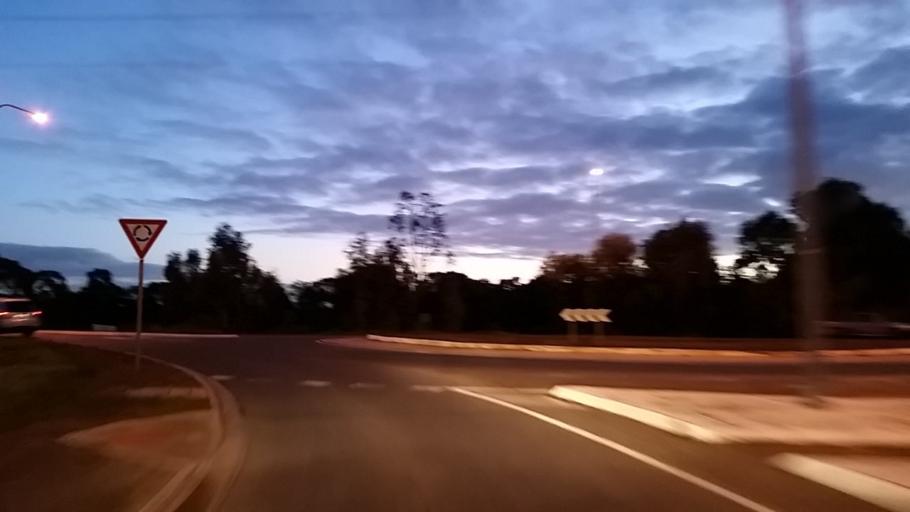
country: AU
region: South Australia
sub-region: Gawler
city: Gawler
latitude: -34.6083
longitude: 138.7302
